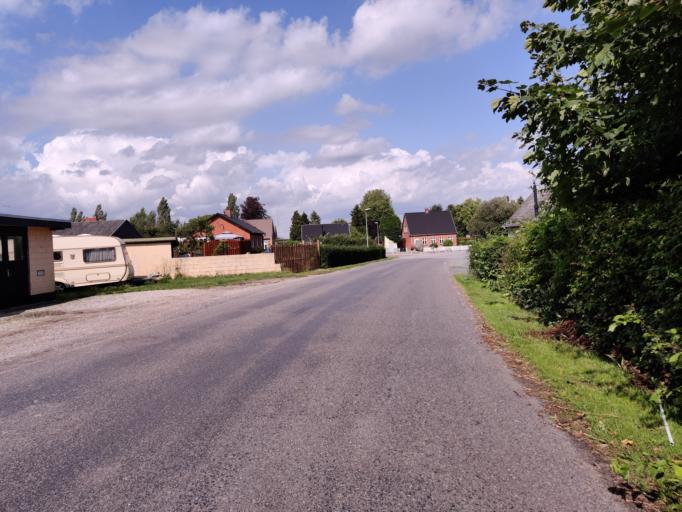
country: DK
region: Zealand
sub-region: Guldborgsund Kommune
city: Nykobing Falster
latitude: 54.6775
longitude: 11.9010
